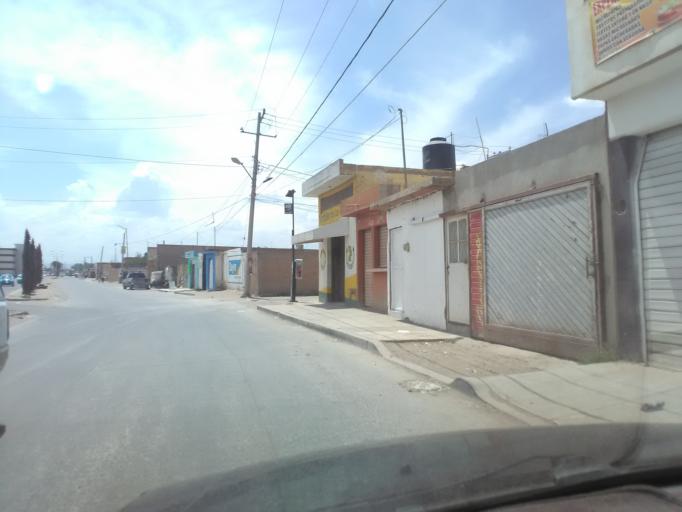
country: MX
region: Durango
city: Victoria de Durango
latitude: 24.0128
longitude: -104.6118
